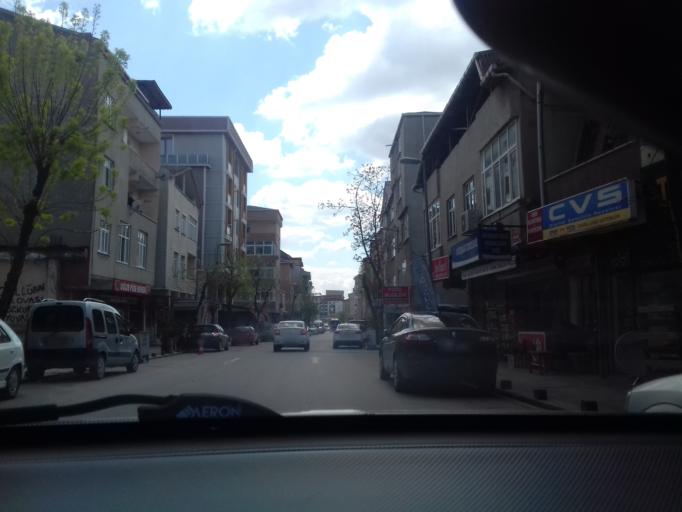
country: TR
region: Istanbul
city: Pendik
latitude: 40.8969
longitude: 29.2744
